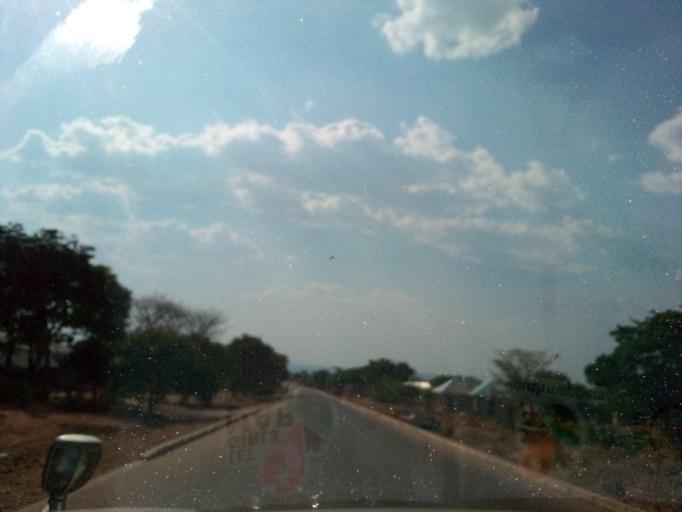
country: ZM
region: Northern
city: Mpika
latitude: -11.8469
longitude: 31.4508
